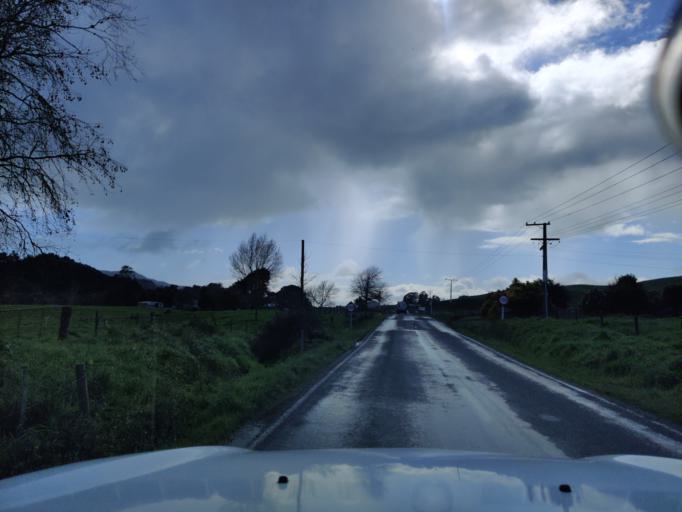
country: NZ
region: Waikato
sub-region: Waikato District
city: Ngaruawahia
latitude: -37.5939
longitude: 175.2079
